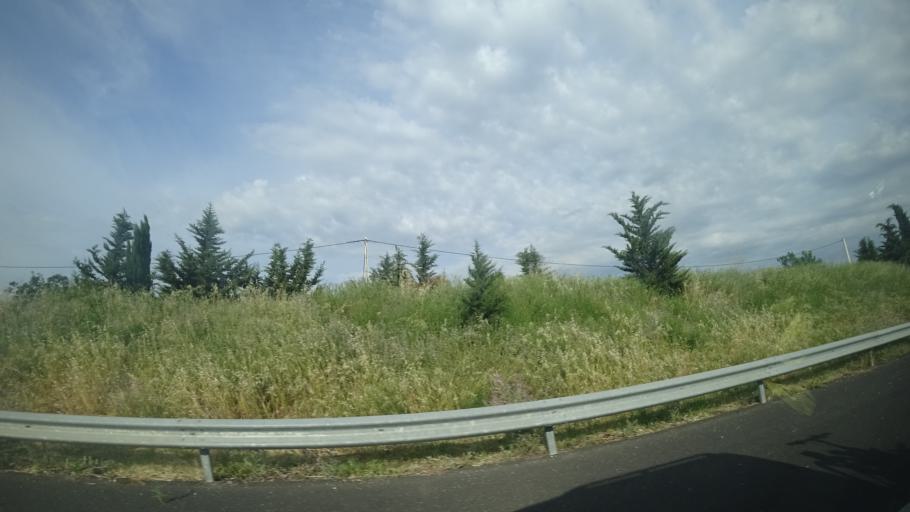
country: FR
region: Languedoc-Roussillon
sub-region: Departement de l'Herault
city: Nebian
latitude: 43.6304
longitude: 3.4488
